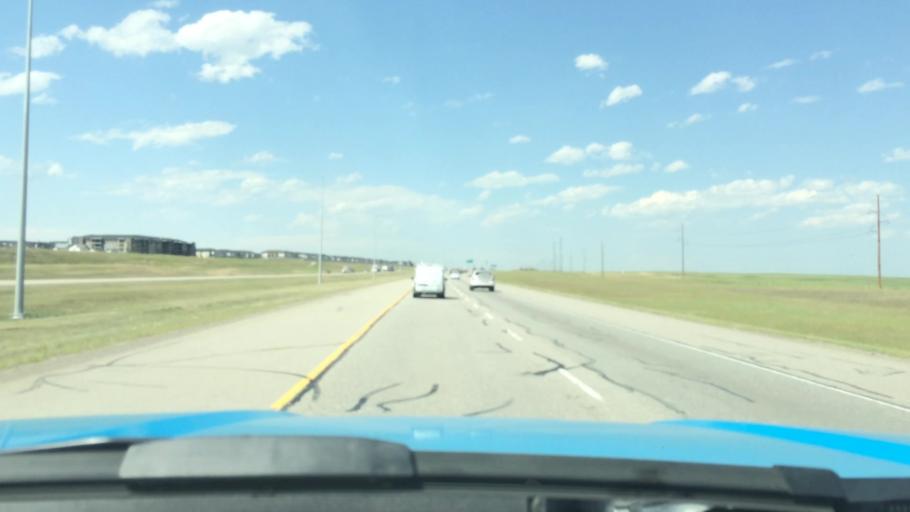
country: CA
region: Alberta
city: Chestermere
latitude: 51.1129
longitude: -113.9204
